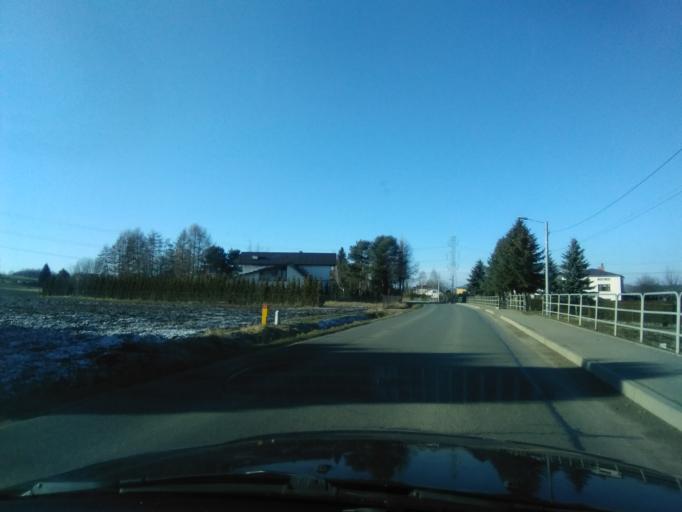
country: PL
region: Subcarpathian Voivodeship
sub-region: Powiat brzozowski
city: Haczow
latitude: 49.6762
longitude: 21.8805
